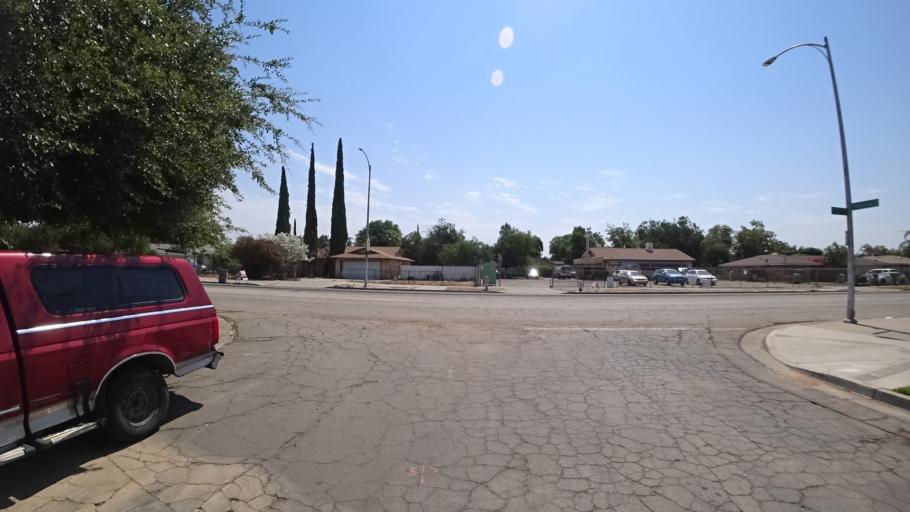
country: US
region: California
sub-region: Fresno County
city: Fresno
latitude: 36.7160
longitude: -119.8000
